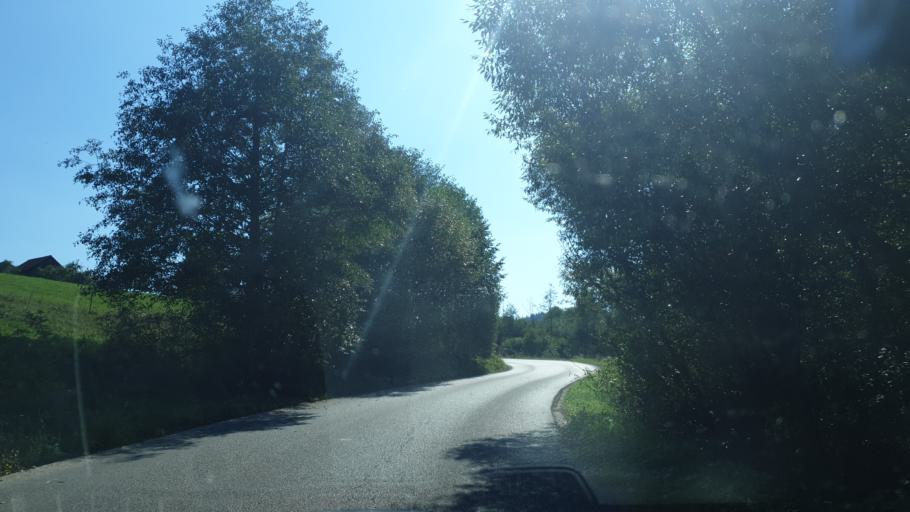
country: RS
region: Central Serbia
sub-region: Zlatiborski Okrug
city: Nova Varos
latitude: 43.4382
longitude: 19.8642
